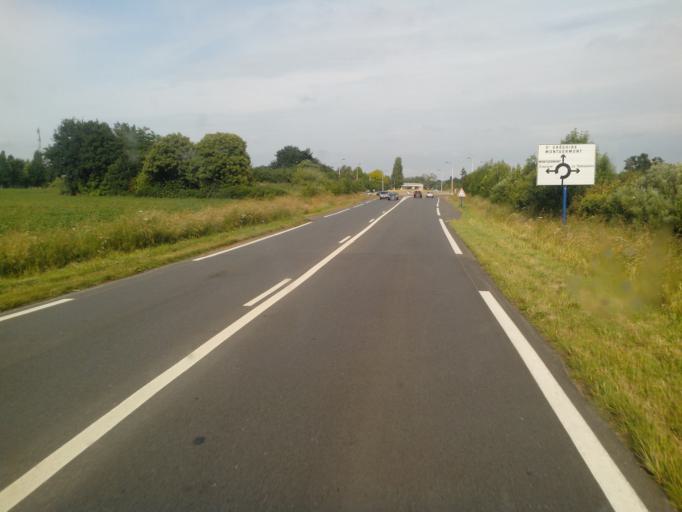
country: FR
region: Brittany
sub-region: Departement d'Ille-et-Vilaine
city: Montgermont
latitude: 48.1503
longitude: -1.7253
